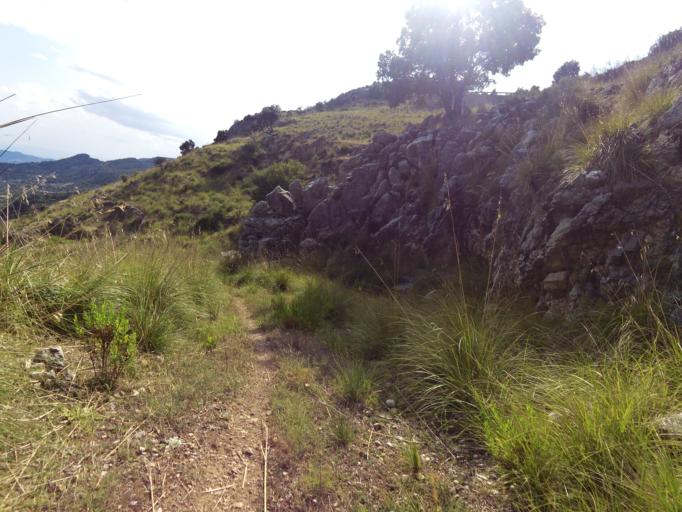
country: IT
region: Calabria
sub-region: Provincia di Reggio Calabria
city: Pazzano
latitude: 38.4658
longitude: 16.4420
